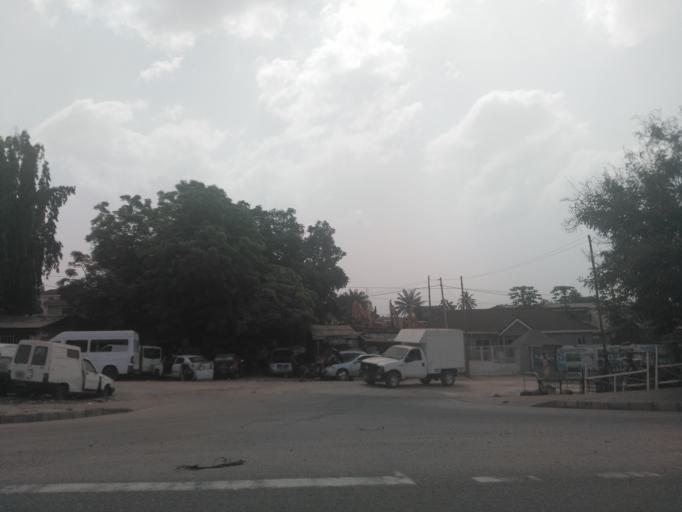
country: GH
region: Greater Accra
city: Dome
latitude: 5.6136
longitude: -0.2236
